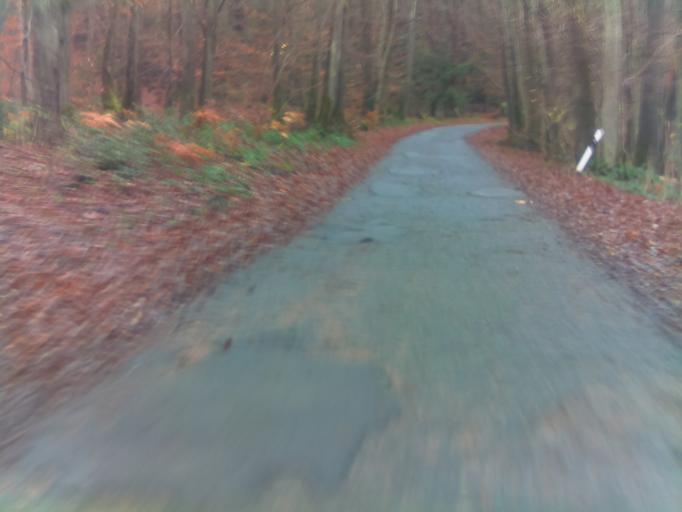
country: DE
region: Baden-Wuerttemberg
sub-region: Karlsruhe Region
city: Heddesbach
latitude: 49.4863
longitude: 8.8612
